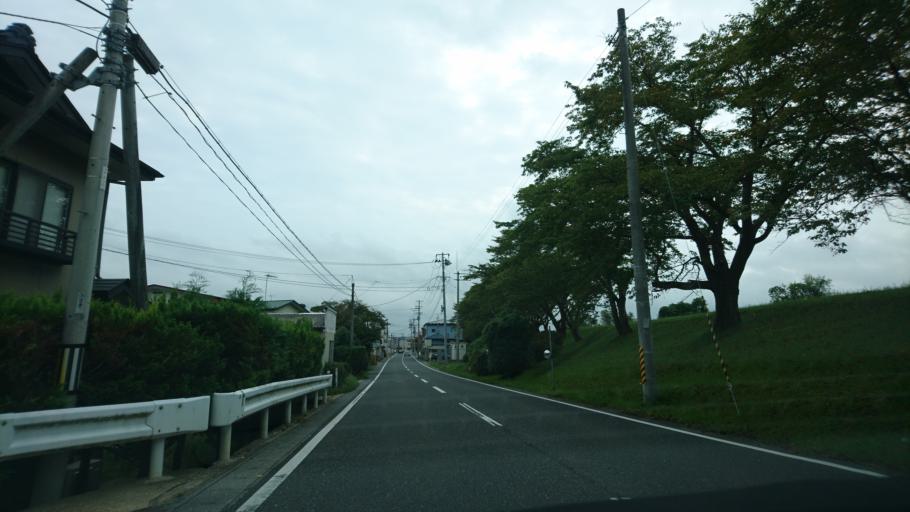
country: JP
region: Iwate
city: Ichinoseki
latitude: 38.7755
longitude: 141.1249
